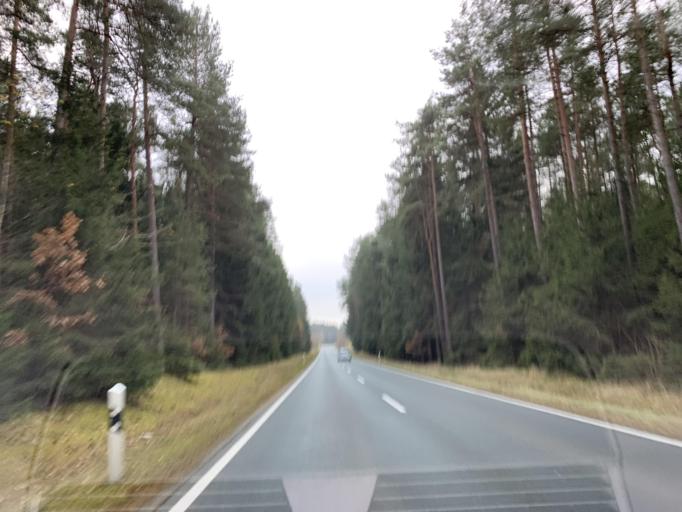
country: DE
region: Bavaria
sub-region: Upper Palatinate
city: Neunburg vorm Wald
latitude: 49.3458
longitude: 12.4242
